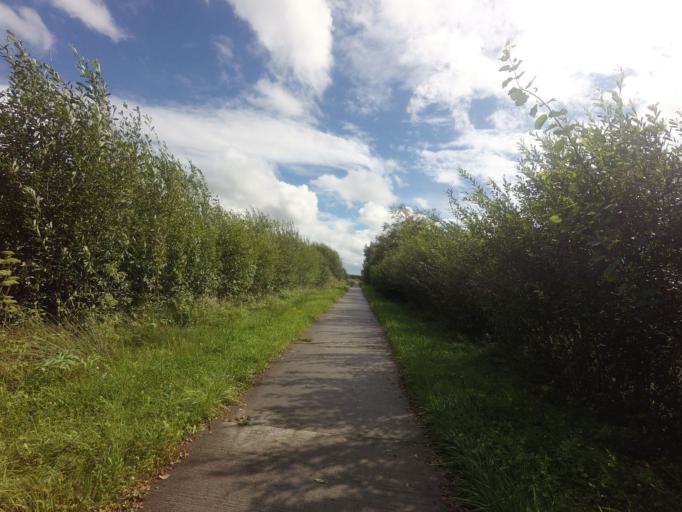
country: NL
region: Groningen
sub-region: Gemeente Leek
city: Leek
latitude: 52.9990
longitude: 6.3510
